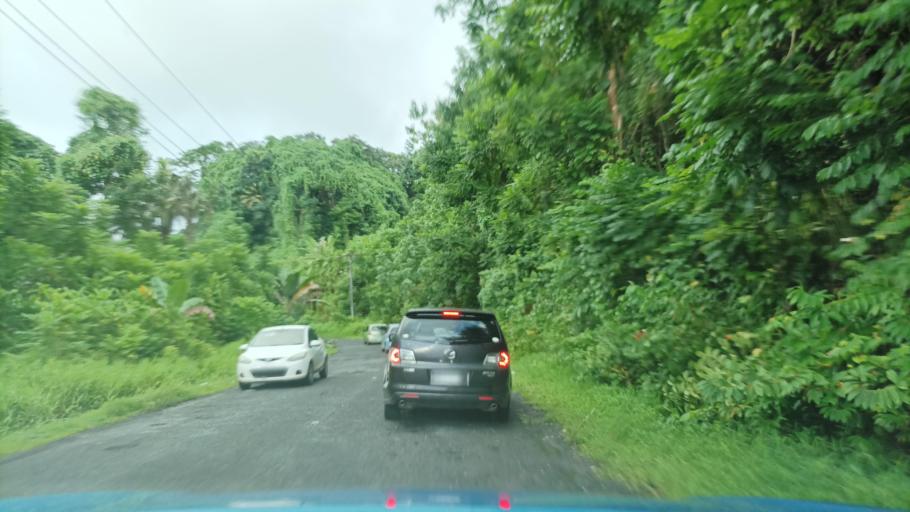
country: FM
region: Pohnpei
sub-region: Kolonia Municipality
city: Kolonia Town
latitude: 6.9473
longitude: 158.1866
